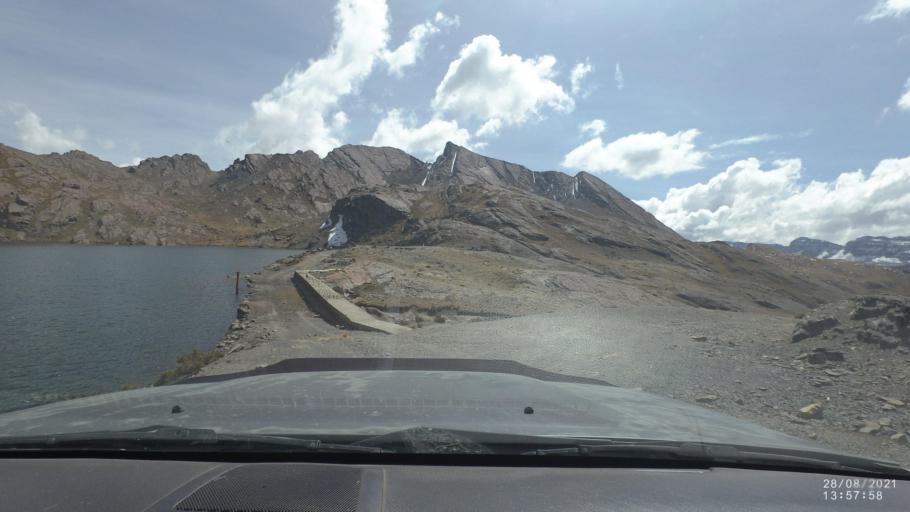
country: BO
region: Cochabamba
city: Sipe Sipe
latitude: -17.2758
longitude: -66.3870
